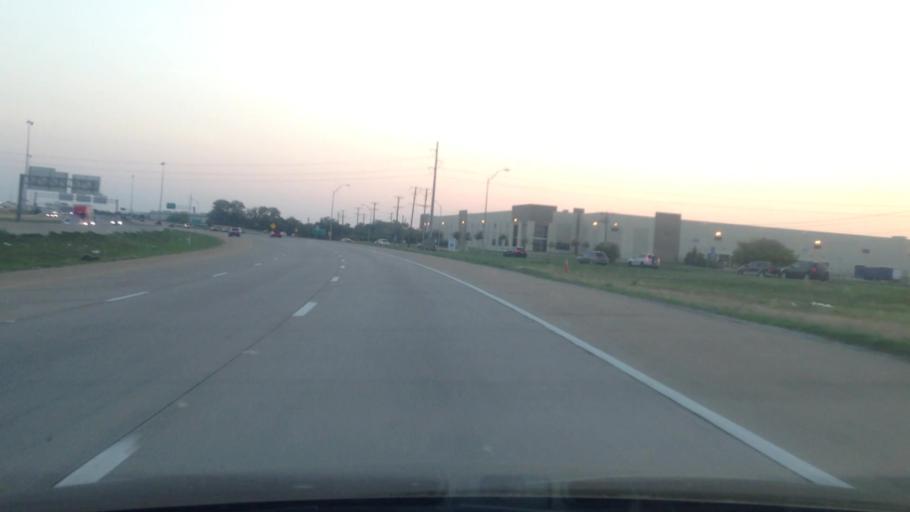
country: US
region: Texas
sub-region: Dallas County
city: Coppell
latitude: 32.9904
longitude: -97.0084
